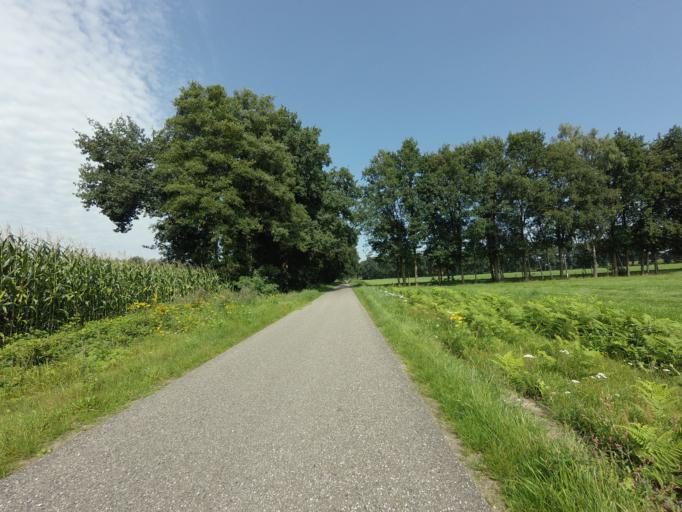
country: NL
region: Overijssel
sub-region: Gemeente Hof van Twente
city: Hengevelde
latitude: 52.1881
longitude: 6.6338
